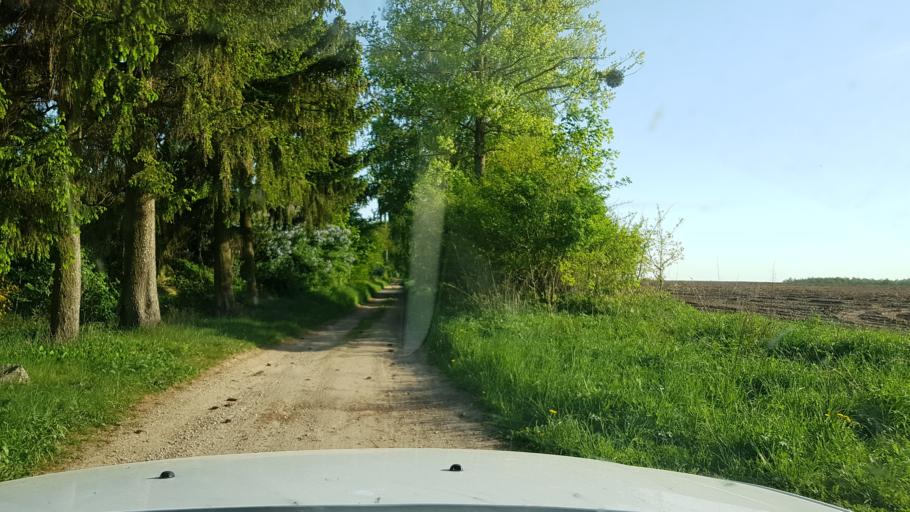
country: PL
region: West Pomeranian Voivodeship
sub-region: Powiat lobeski
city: Resko
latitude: 53.6945
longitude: 15.3359
